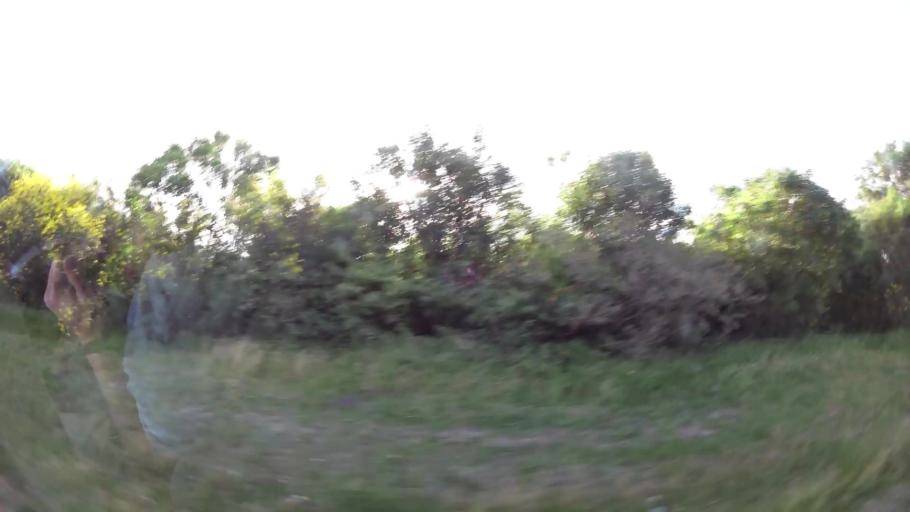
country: UY
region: Montevideo
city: Montevideo
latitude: -34.8941
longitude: -56.2612
